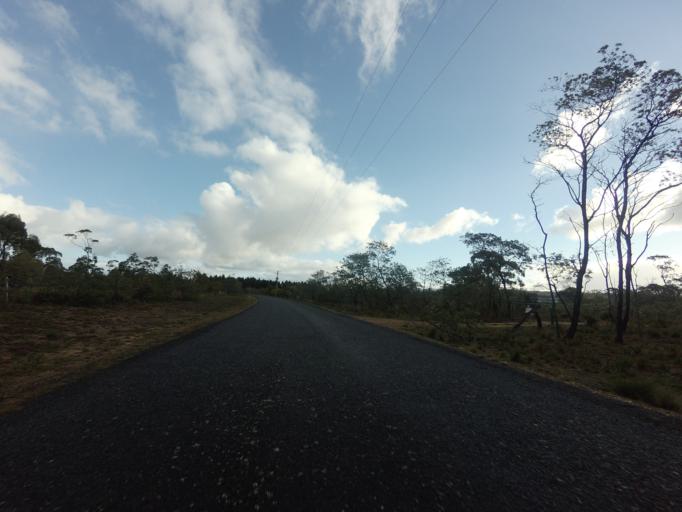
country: AU
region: Tasmania
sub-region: Break O'Day
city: St Helens
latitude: -42.1026
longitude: 148.0733
